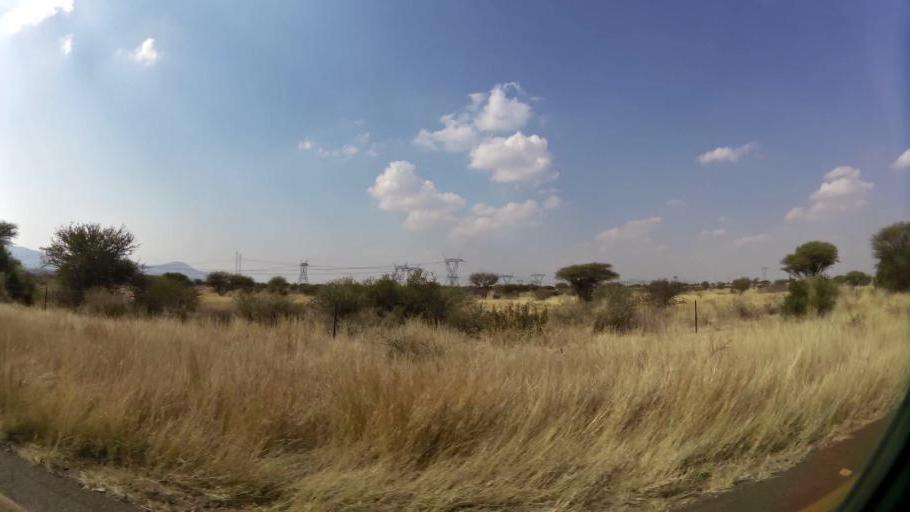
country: ZA
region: North-West
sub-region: Bojanala Platinum District Municipality
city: Mogwase
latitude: -25.4025
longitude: 27.0738
